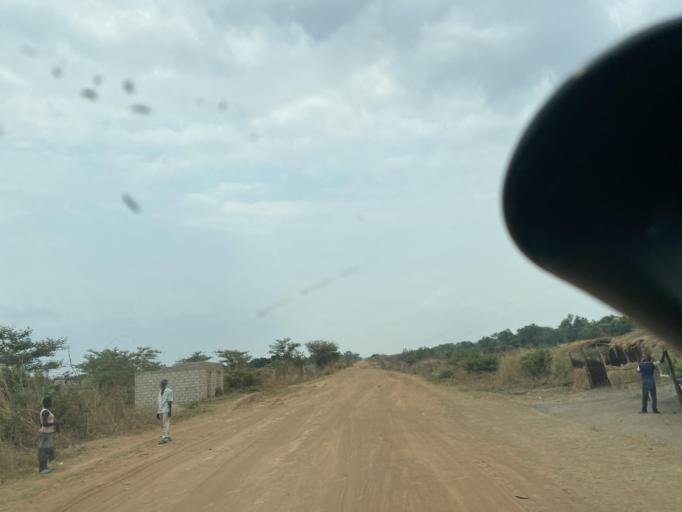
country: ZM
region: Lusaka
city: Lusaka
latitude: -15.2089
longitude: 28.3398
